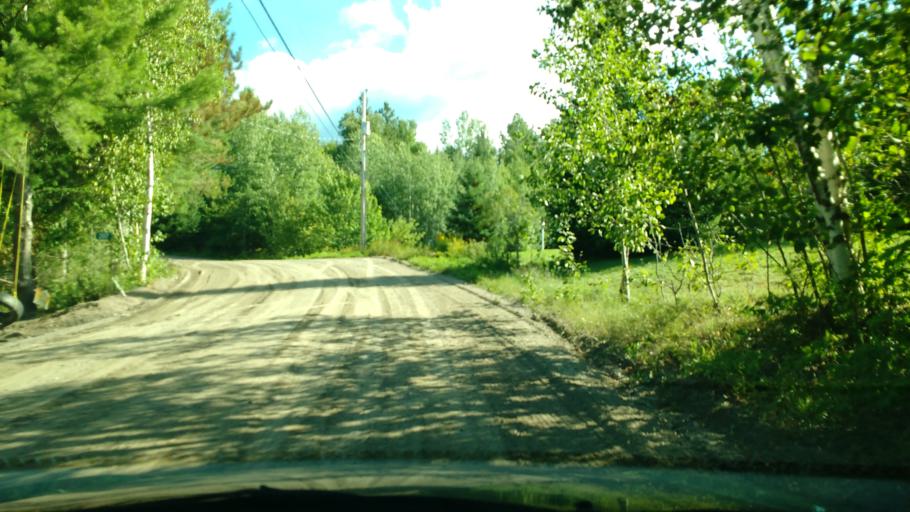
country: CA
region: Ontario
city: Powassan
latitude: 46.1880
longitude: -79.2813
